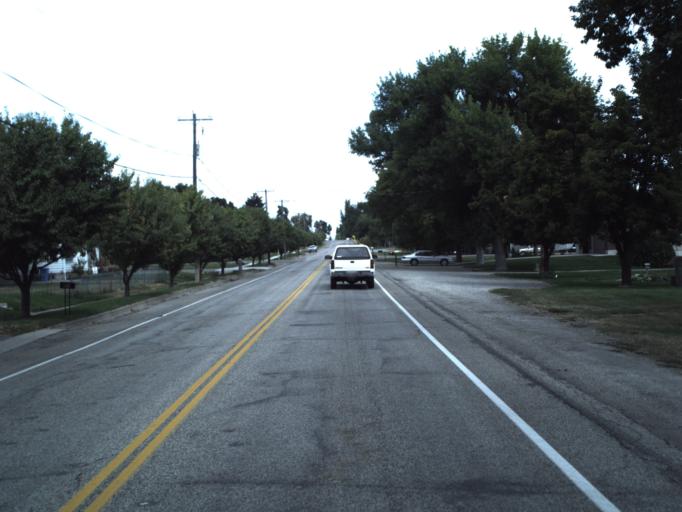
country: US
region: Utah
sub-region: Cache County
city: Wellsville
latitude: 41.6438
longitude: -111.9342
